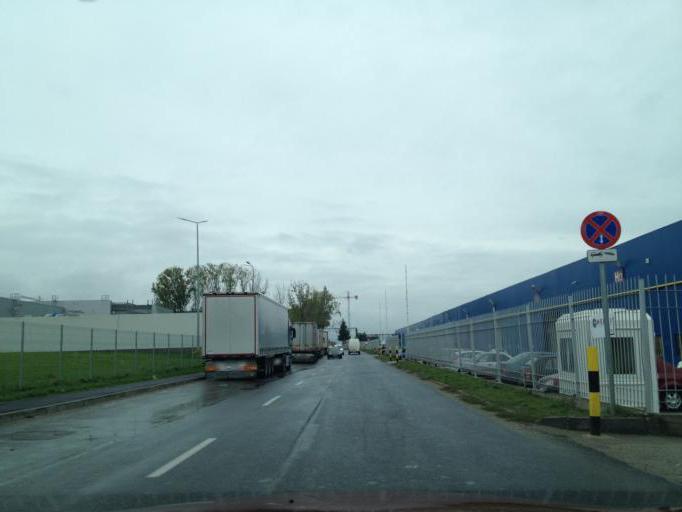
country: RO
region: Brasov
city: Brasov
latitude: 45.6746
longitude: 25.6181
